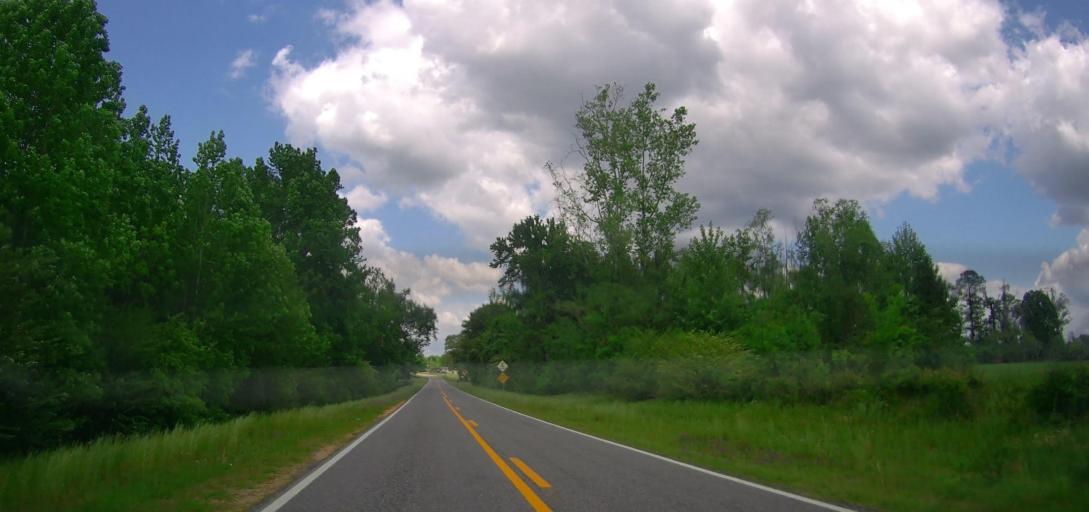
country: US
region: Georgia
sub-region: Laurens County
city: East Dublin
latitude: 32.5512
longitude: -82.8177
